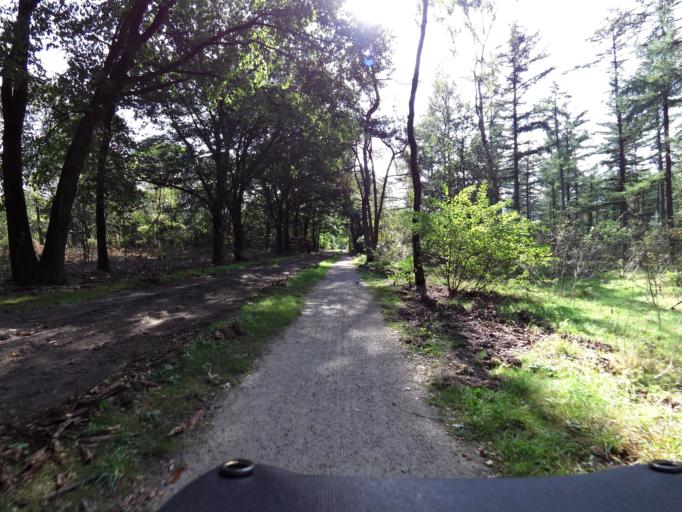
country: NL
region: Gelderland
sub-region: Gemeente Apeldoorn
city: Uddel
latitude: 52.2117
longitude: 5.7694
